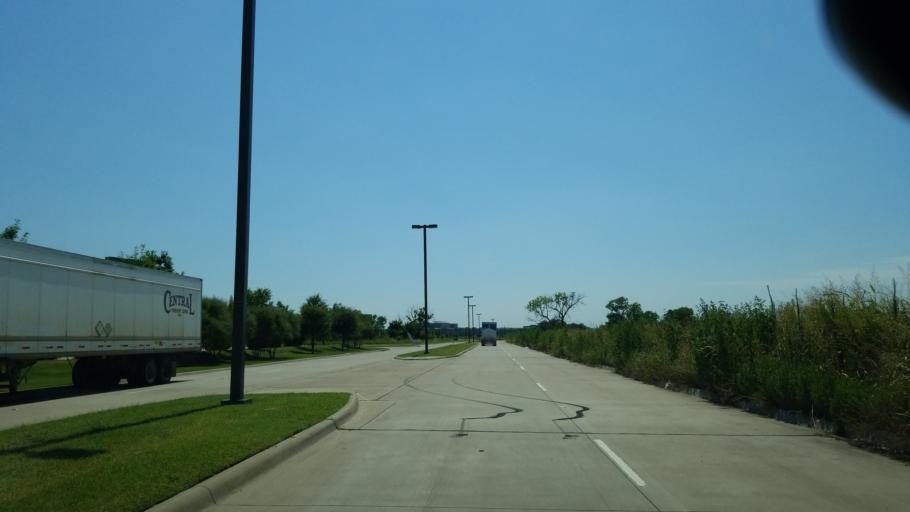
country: US
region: Texas
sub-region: Dallas County
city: Farmers Branch
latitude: 32.9141
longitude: -96.9022
